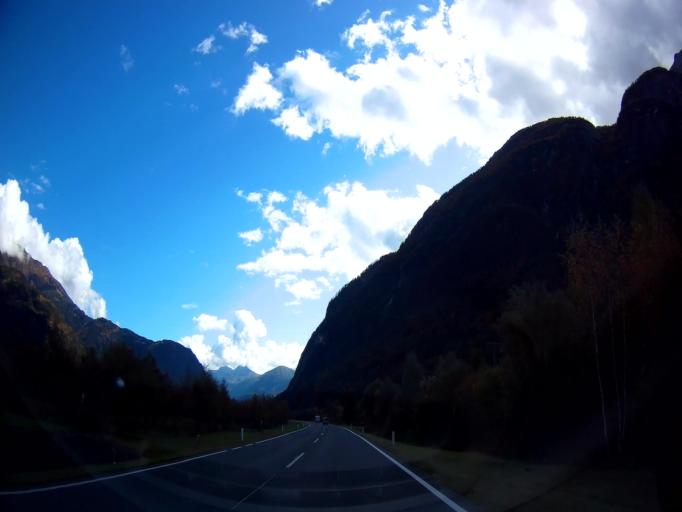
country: AT
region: Tyrol
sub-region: Politischer Bezirk Lienz
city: Nikolsdorf
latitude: 46.7866
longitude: 12.8799
